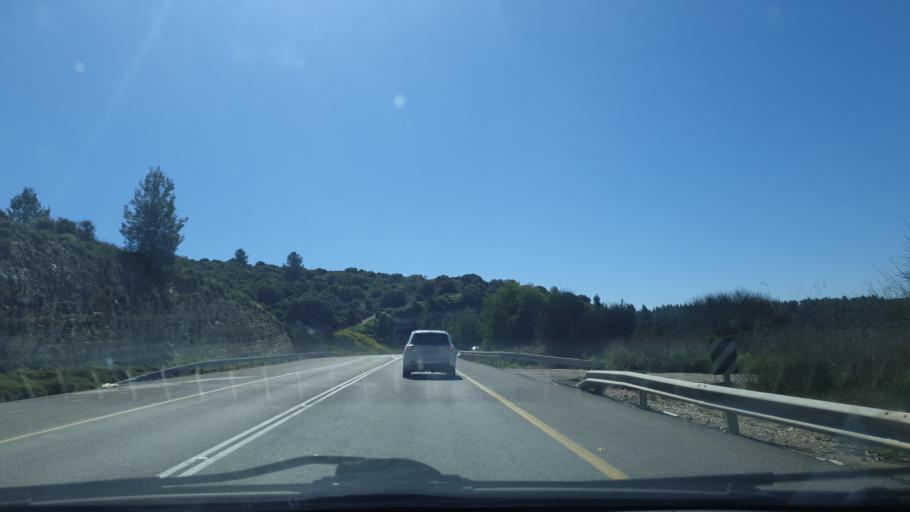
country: IL
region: Jerusalem
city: Bet Shemesh
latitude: 31.6958
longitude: 34.9429
